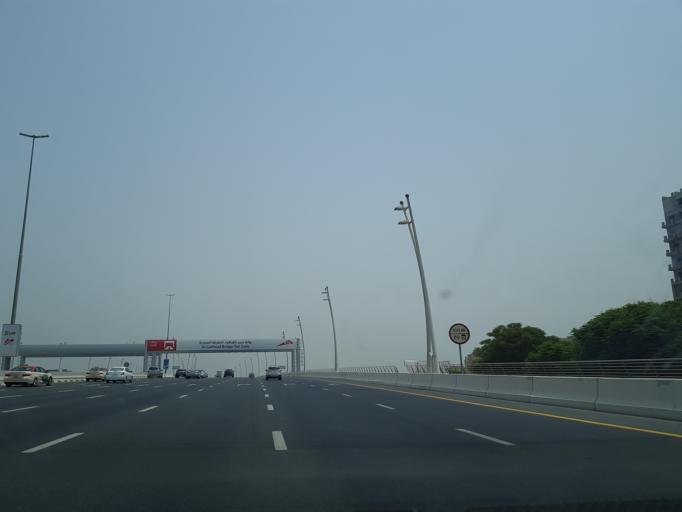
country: AE
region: Ash Shariqah
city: Sharjah
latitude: 25.2298
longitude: 55.3348
